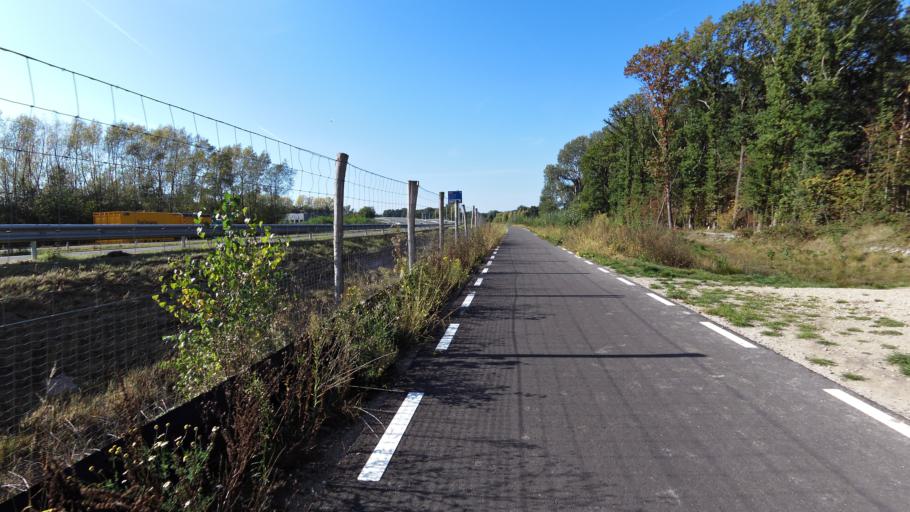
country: NL
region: Limburg
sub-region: Gemeente Onderbanken
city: Schinveld
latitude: 50.9593
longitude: 5.9822
